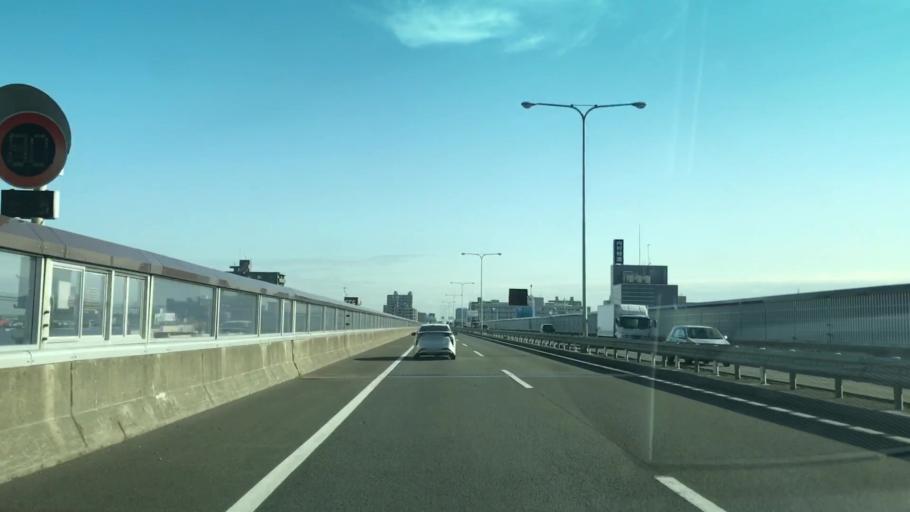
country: JP
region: Hokkaido
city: Sapporo
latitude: 43.1033
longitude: 141.3572
